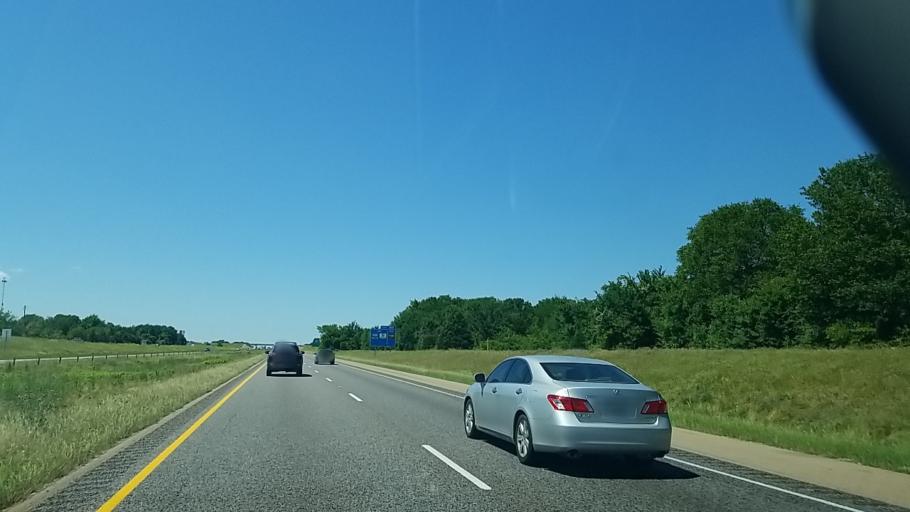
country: US
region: Texas
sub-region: Freestone County
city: Fairfield
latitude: 31.5878
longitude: -96.1507
